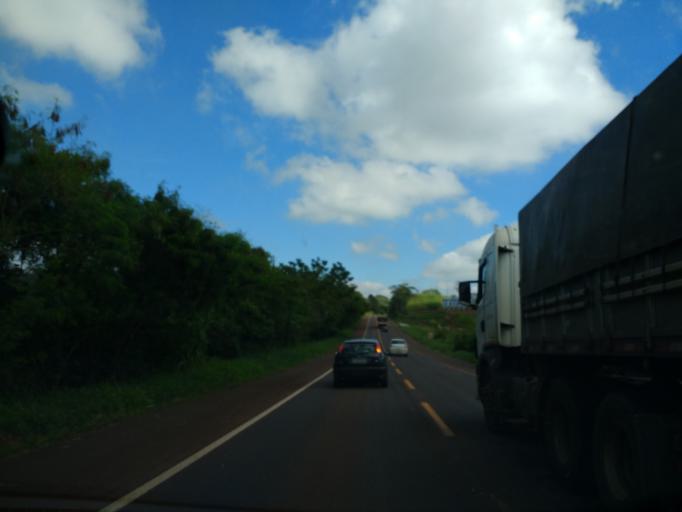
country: BR
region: Parana
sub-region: Cruzeiro Do Oeste
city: Cruzeiro do Oeste
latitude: -23.7700
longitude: -53.1605
